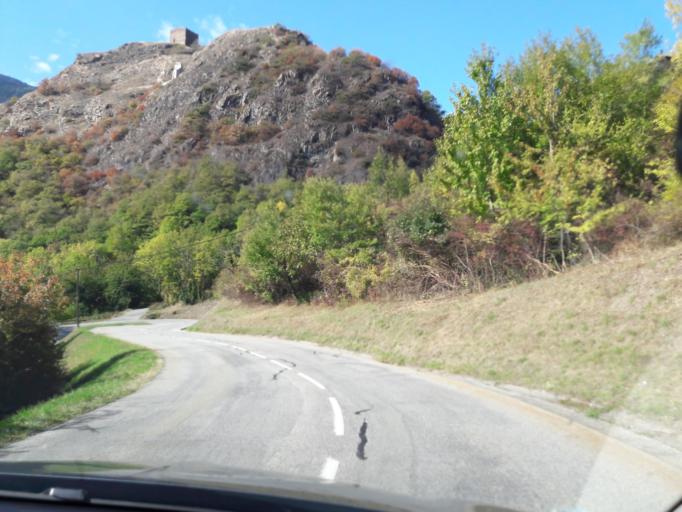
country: FR
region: Rhone-Alpes
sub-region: Departement de la Savoie
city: Saint-Jean-de-Maurienne
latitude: 45.3031
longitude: 6.3647
